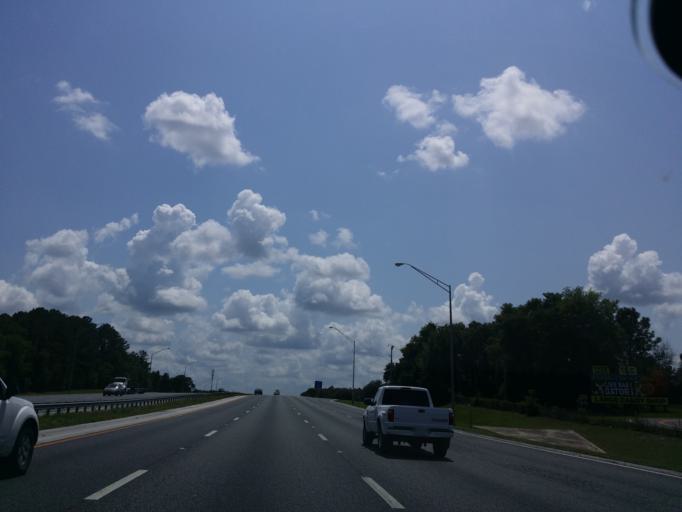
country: US
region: Florida
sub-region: Marion County
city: Ocala
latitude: 29.0997
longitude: -82.1850
